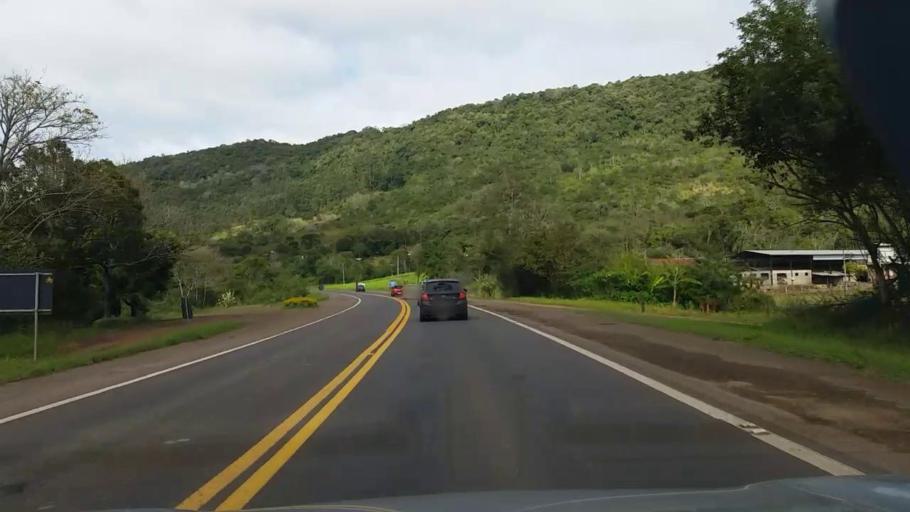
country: BR
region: Rio Grande do Sul
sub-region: Arroio Do Meio
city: Arroio do Meio
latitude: -29.3304
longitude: -52.1013
